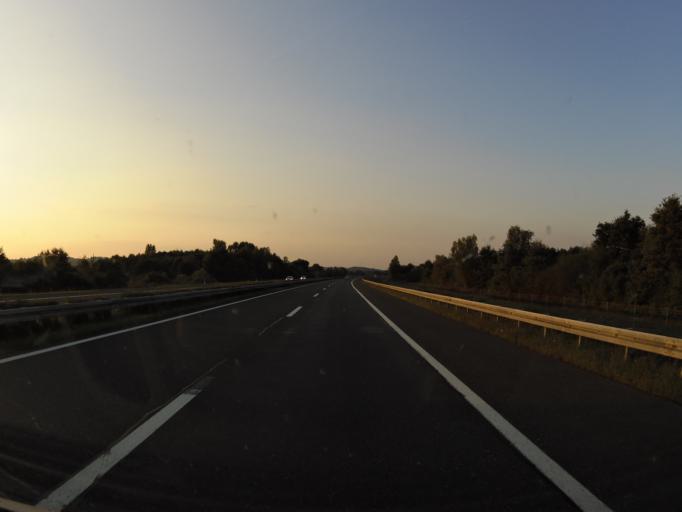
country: HR
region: Zagrebacka
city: Pojatno
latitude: 45.8960
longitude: 15.8226
